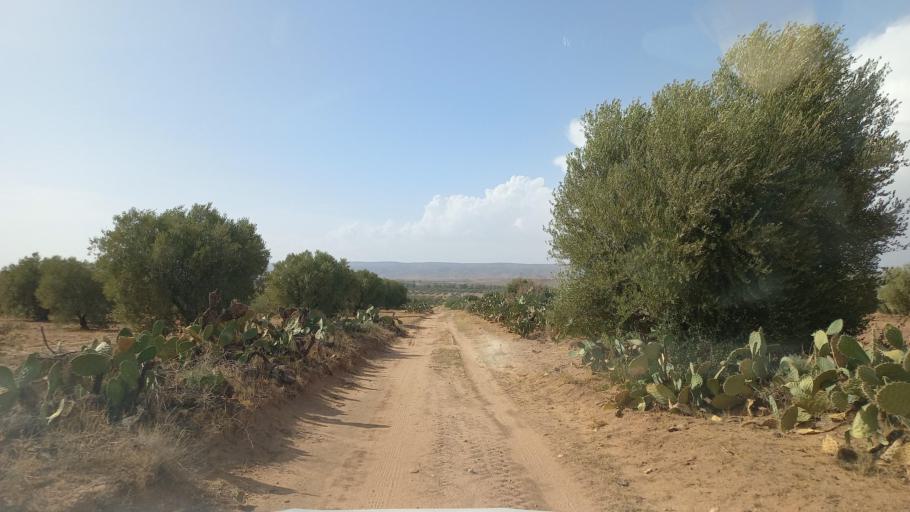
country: TN
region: Al Qasrayn
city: Kasserine
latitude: 35.2125
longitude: 8.9525
